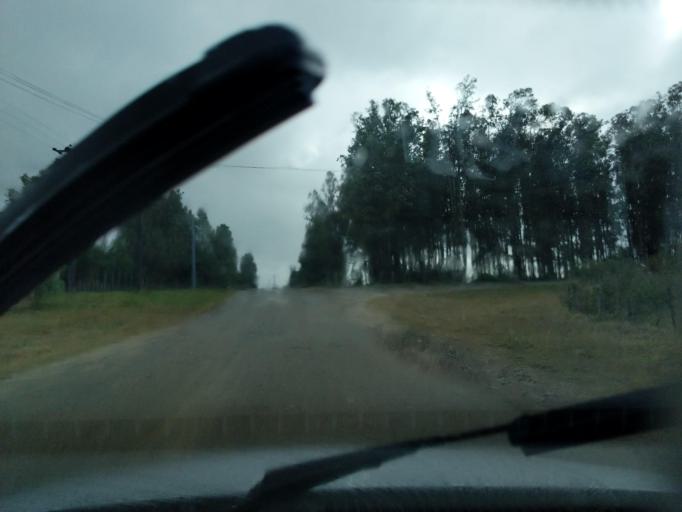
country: UY
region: Florida
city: Florida
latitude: -34.0945
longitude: -56.1694
